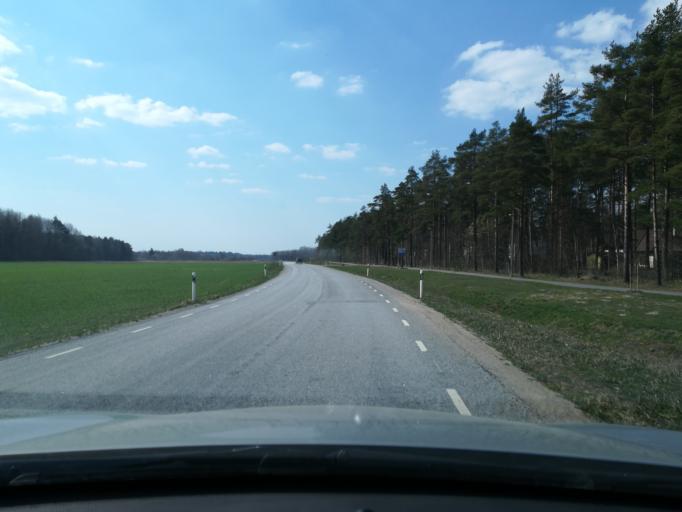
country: EE
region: Harju
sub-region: Saue vald
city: Laagri
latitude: 59.3450
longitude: 24.5964
